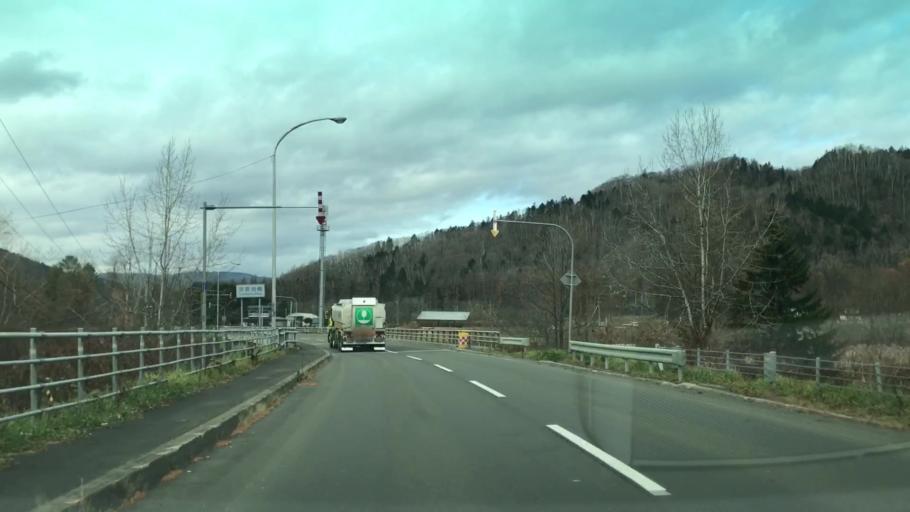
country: JP
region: Hokkaido
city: Shimo-furano
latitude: 42.9491
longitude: 142.4422
